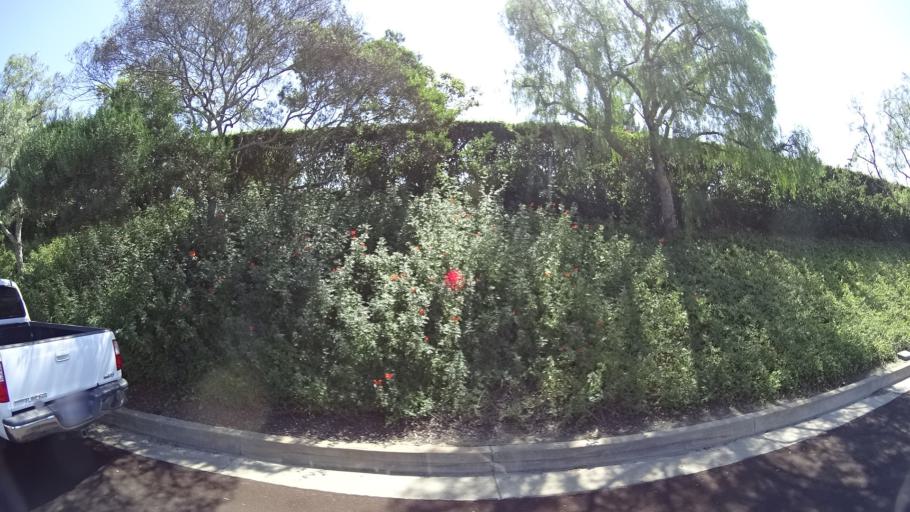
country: US
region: California
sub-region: Orange County
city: San Clemente
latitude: 33.4621
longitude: -117.6223
